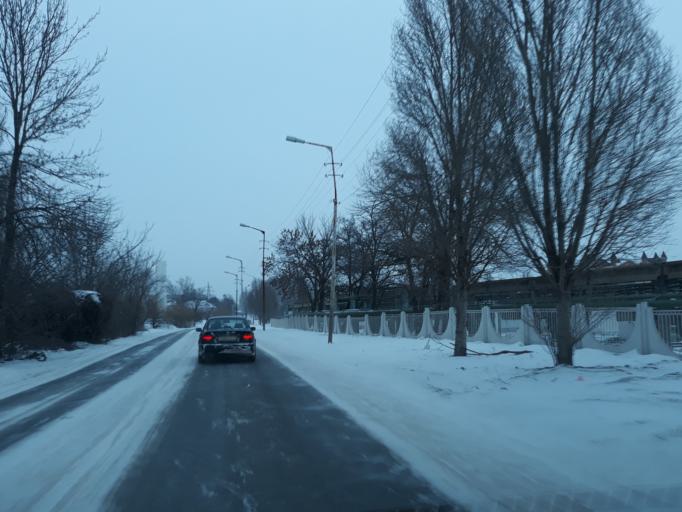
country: RU
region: Rostov
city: Taganrog
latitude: 47.2477
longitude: 38.9326
